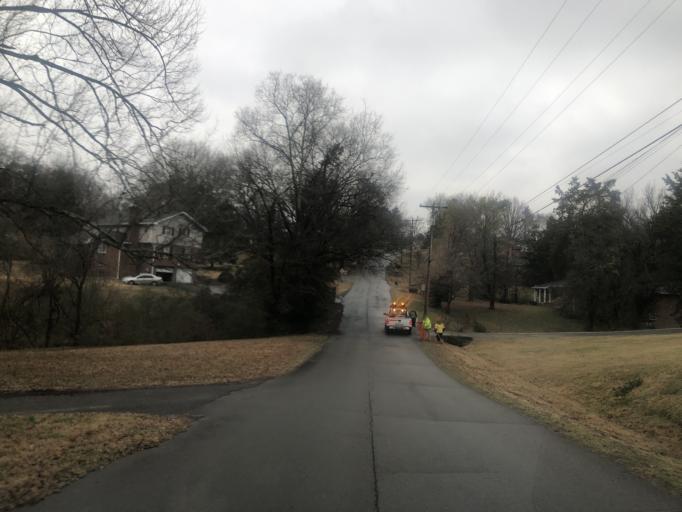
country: US
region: Tennessee
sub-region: Davidson County
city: Nashville
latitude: 36.1639
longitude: -86.6922
